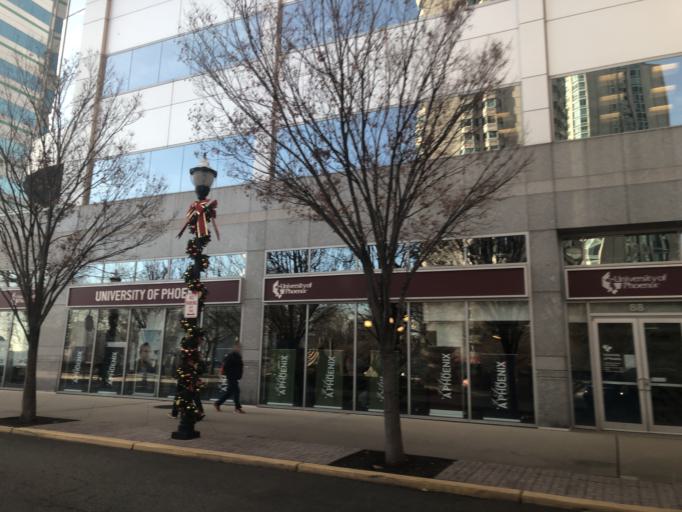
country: US
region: New Jersey
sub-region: Hudson County
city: Hoboken
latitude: 40.7269
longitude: -74.0328
